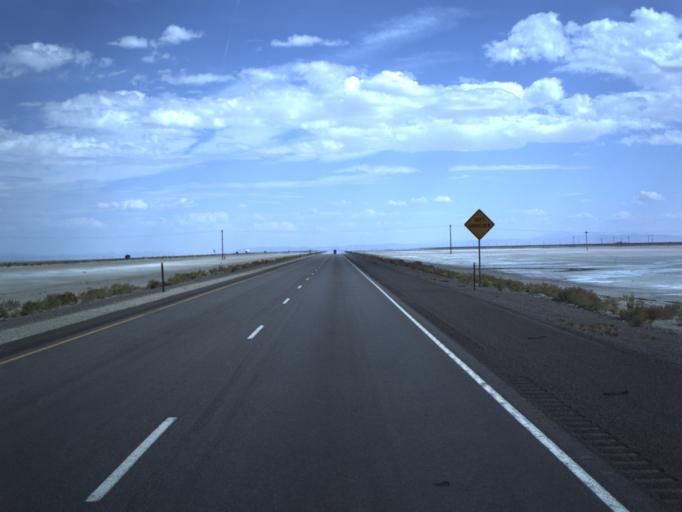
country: US
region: Utah
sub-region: Tooele County
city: Wendover
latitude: 40.7368
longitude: -113.7703
